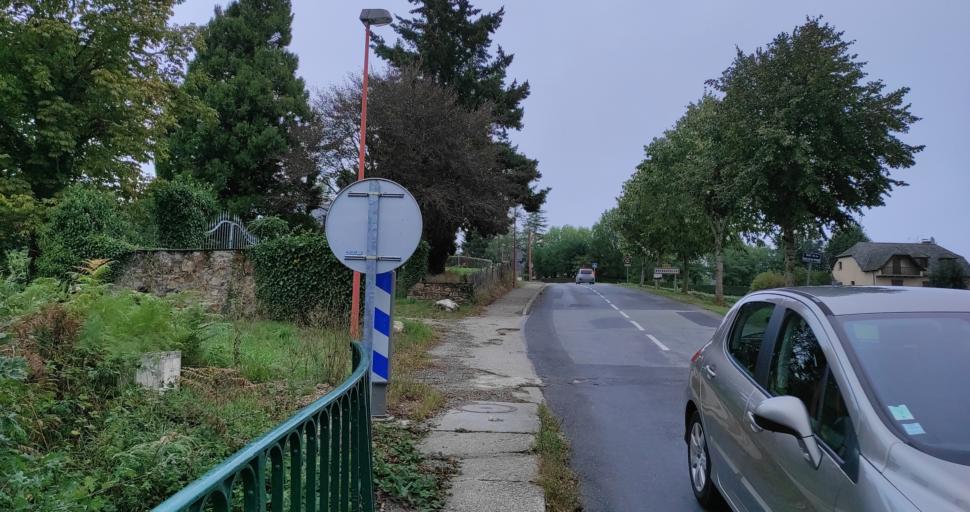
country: FR
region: Midi-Pyrenees
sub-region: Departement de l'Aveyron
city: Baraqueville
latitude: 44.2724
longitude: 2.4353
